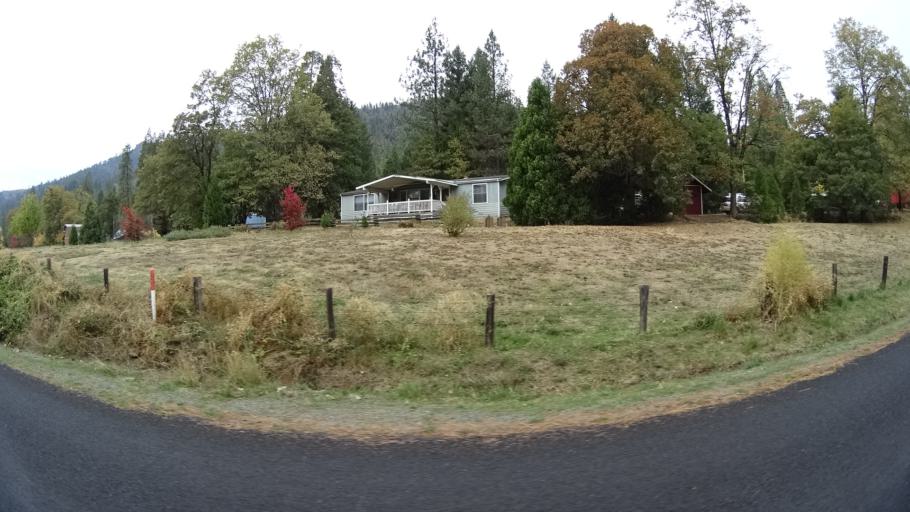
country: US
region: California
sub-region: Siskiyou County
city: Happy Camp
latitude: 41.8467
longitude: -123.1887
